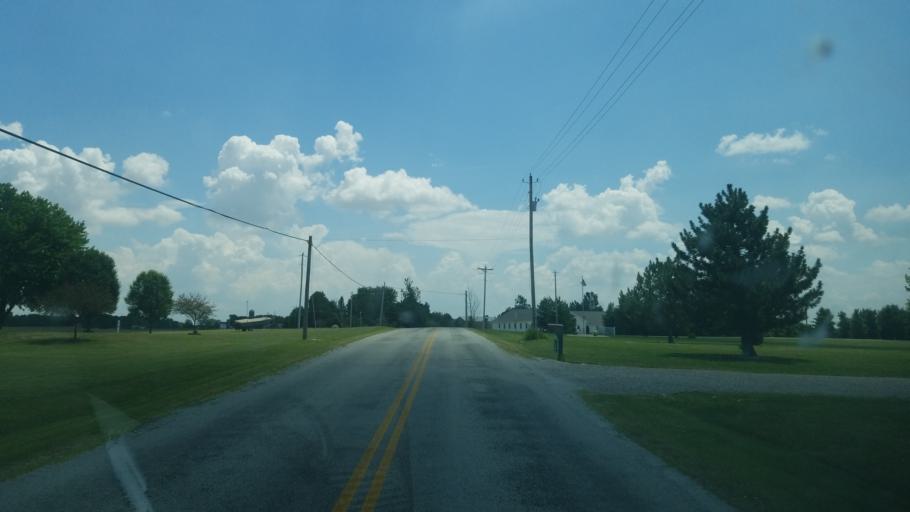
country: US
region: Ohio
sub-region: Hardin County
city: Kenton
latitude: 40.6612
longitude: -83.6562
